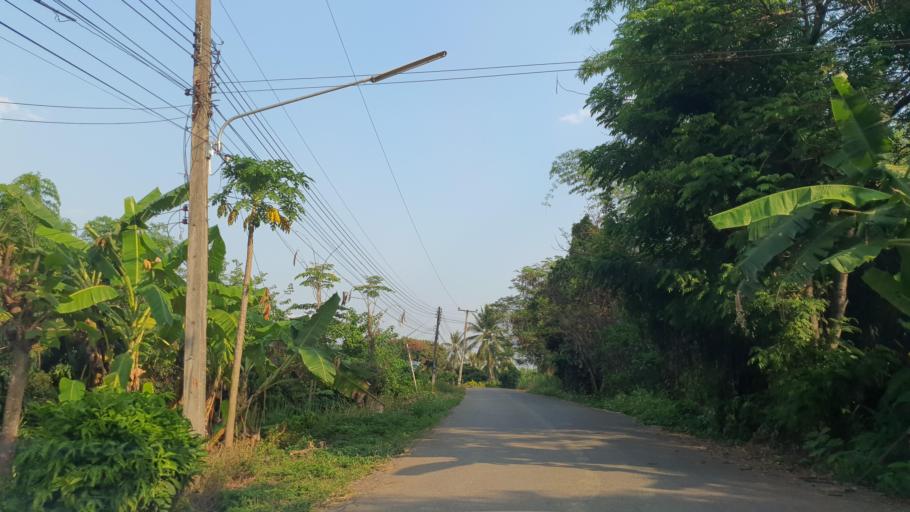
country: TH
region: Chiang Mai
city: Mae Wang
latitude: 18.6789
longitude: 98.8103
